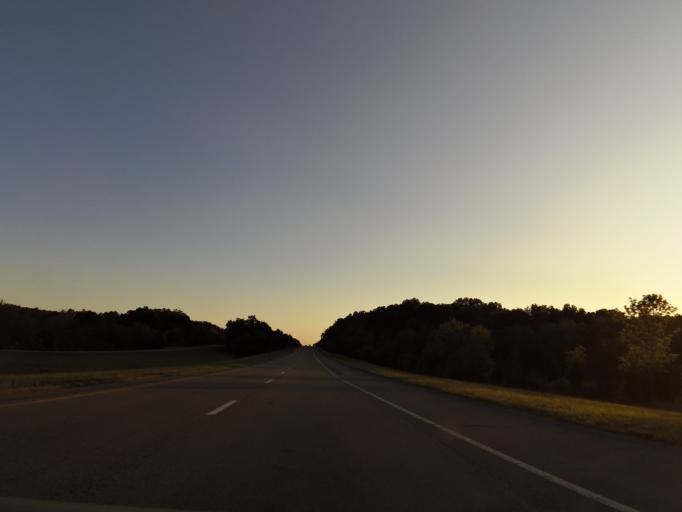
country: US
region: Tennessee
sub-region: Hawkins County
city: Surgoinsville
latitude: 36.3202
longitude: -82.8398
